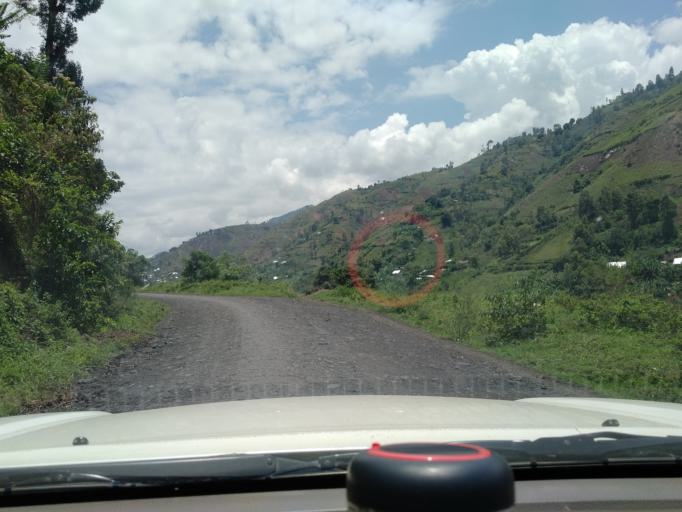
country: CD
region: Nord Kivu
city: Sake
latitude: -1.7450
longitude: 28.9896
